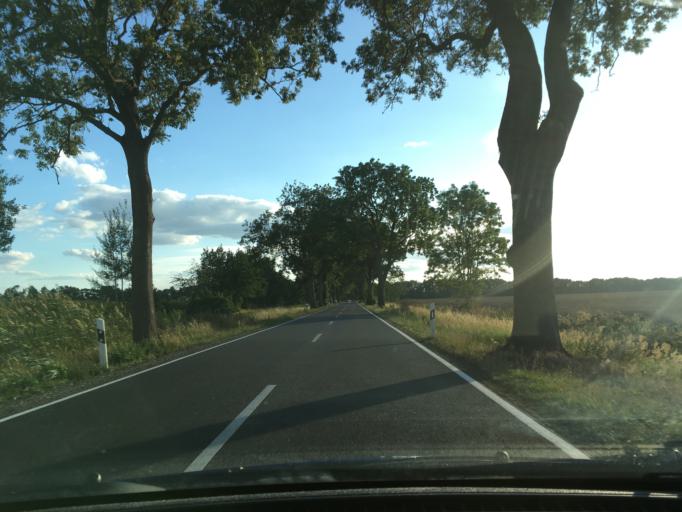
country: DE
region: Mecklenburg-Vorpommern
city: Neu Kaliss
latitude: 53.1719
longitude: 11.2808
